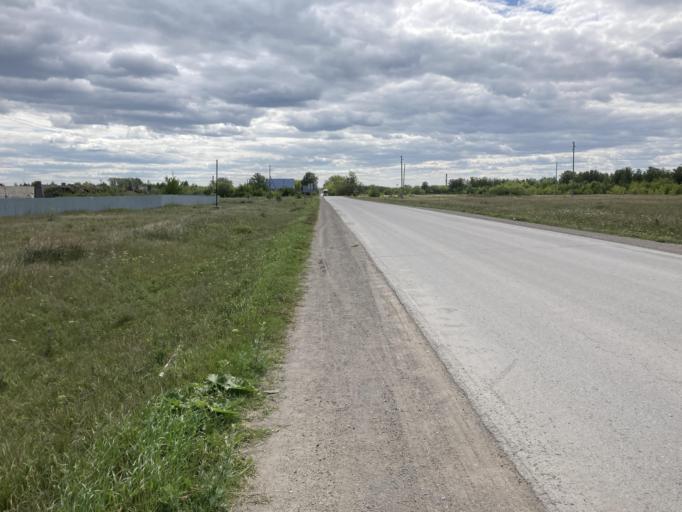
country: RU
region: Sverdlovsk
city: Bogdanovich
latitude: 56.7944
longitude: 62.0685
